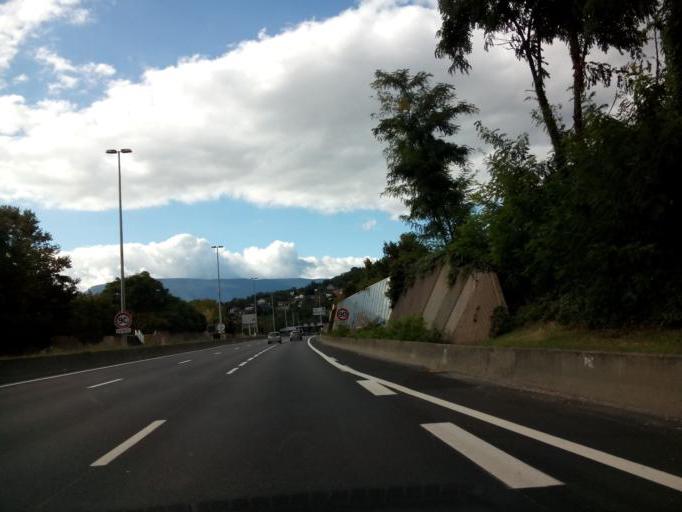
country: FR
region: Rhone-Alpes
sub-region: Departement de la Savoie
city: Chambery
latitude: 45.5696
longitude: 5.9402
